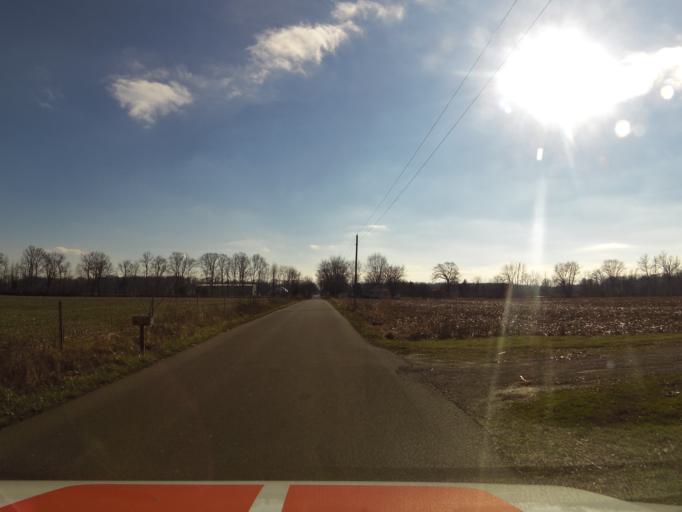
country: US
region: Indiana
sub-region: Jennings County
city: Country Squire Lakes
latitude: 38.9786
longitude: -85.7776
